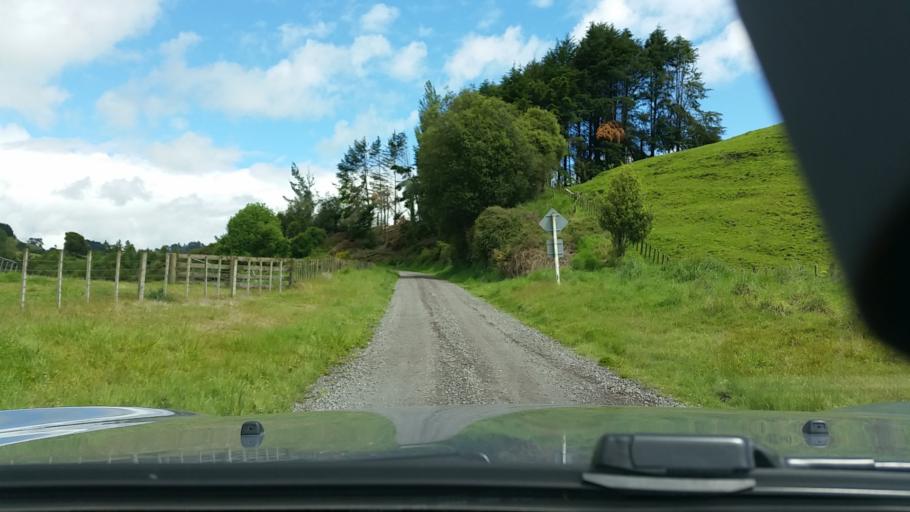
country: NZ
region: Bay of Plenty
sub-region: Rotorua District
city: Rotorua
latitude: -38.4448
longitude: 176.2884
